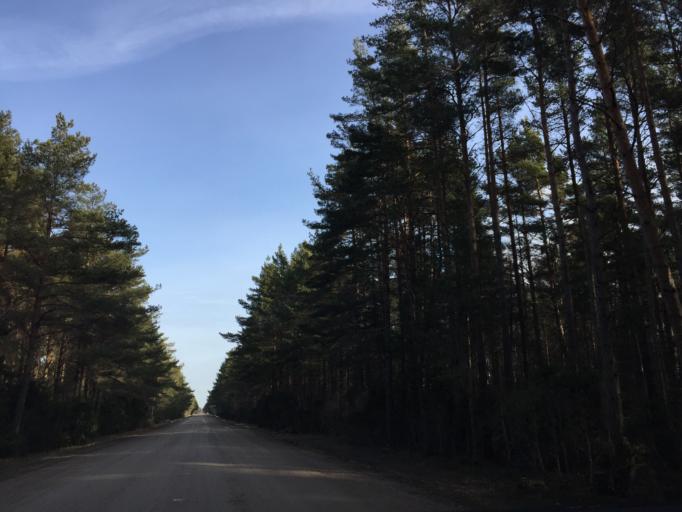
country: EE
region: Saare
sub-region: Kuressaare linn
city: Kuressaare
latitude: 58.2965
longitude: 21.9491
